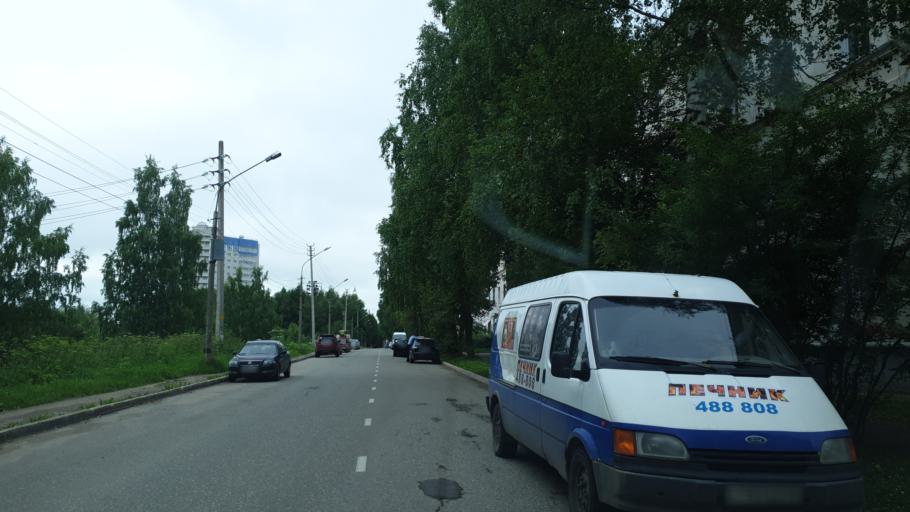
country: RU
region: Komi Republic
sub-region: Syktyvdinskiy Rayon
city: Syktyvkar
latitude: 61.6637
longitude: 50.8252
